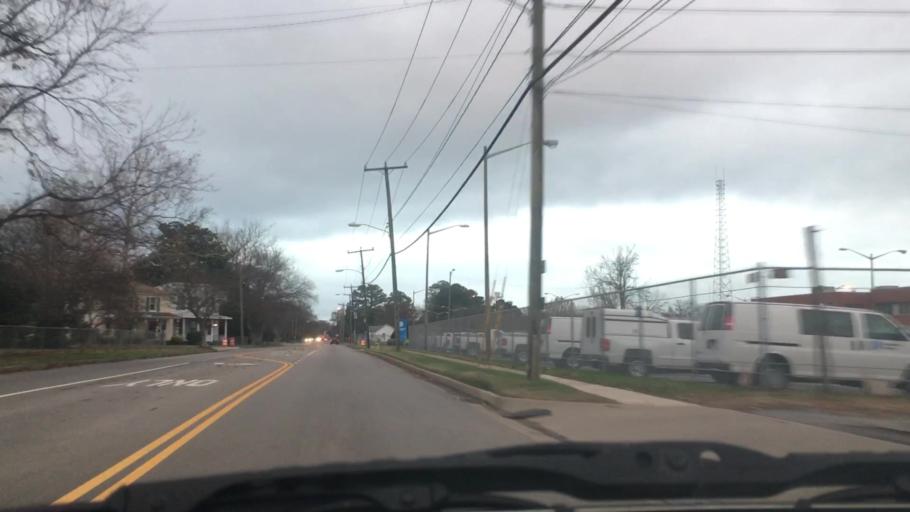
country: US
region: Virginia
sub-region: City of Norfolk
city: Norfolk
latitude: 36.8792
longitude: -76.2536
